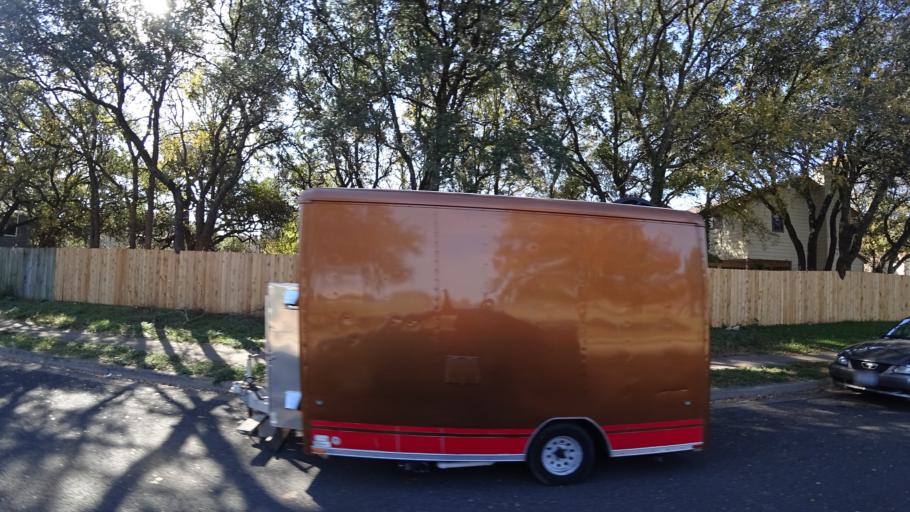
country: US
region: Texas
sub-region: Travis County
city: Barton Creek
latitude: 30.2308
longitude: -97.8446
